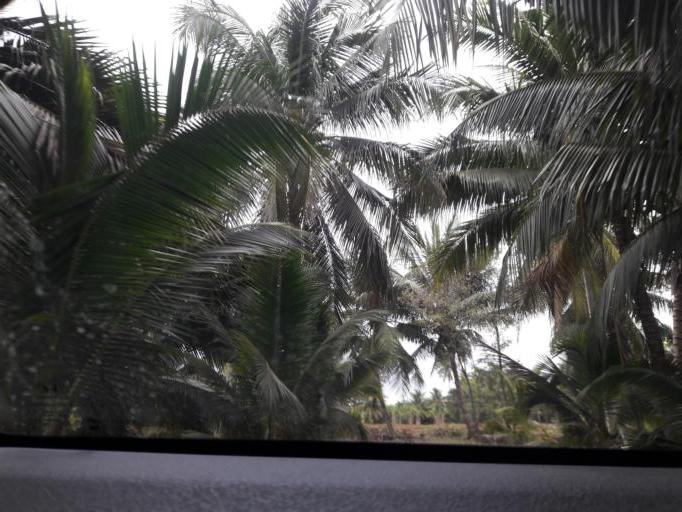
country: TH
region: Ratchaburi
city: Damnoen Saduak
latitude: 13.5668
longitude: 99.9993
